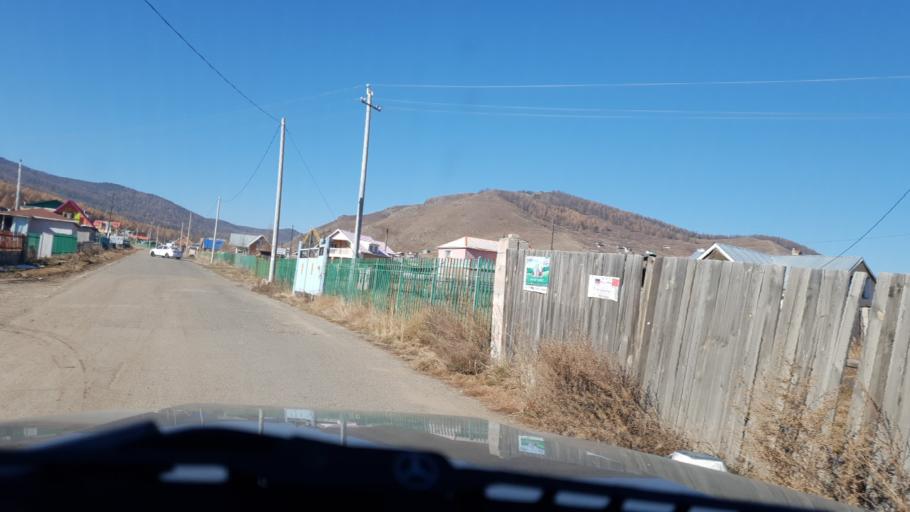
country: MN
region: Ulaanbaatar
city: Ulaanbaatar
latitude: 48.0506
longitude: 106.8972
